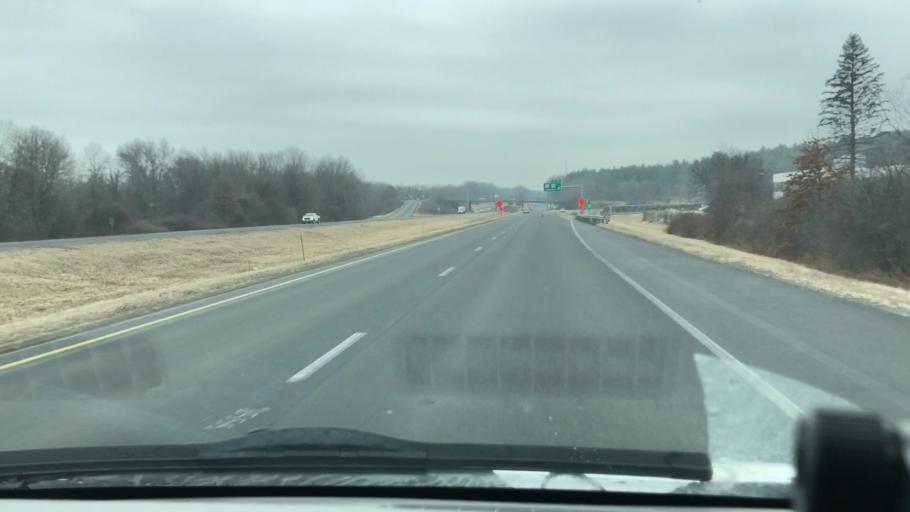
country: US
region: Massachusetts
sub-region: Hampshire County
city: Hatfield
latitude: 42.3660
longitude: -72.6352
